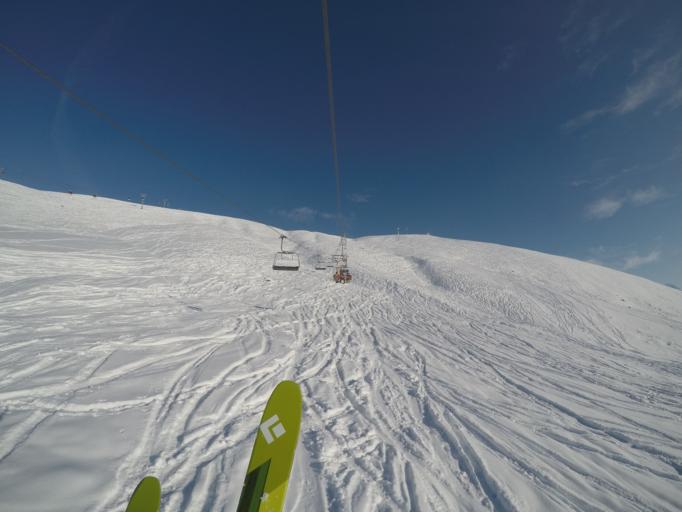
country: GE
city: Gudauri
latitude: 42.4830
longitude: 44.4949
